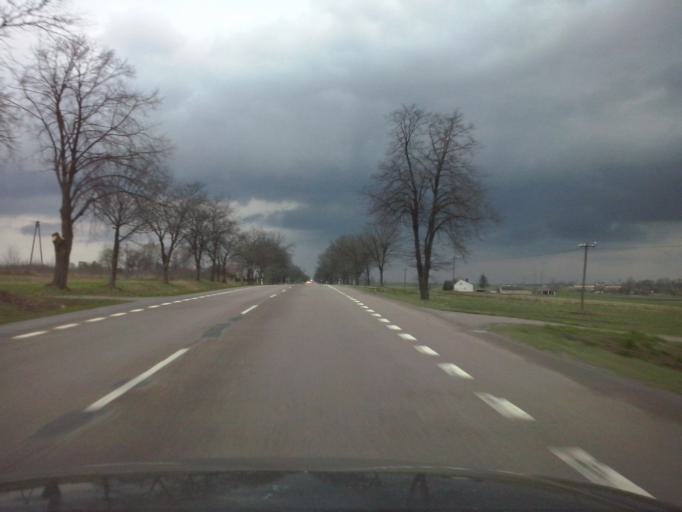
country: PL
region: Lublin Voivodeship
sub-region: Powiat chelmski
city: Rejowiec Fabryczny
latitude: 51.1762
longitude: 23.2404
